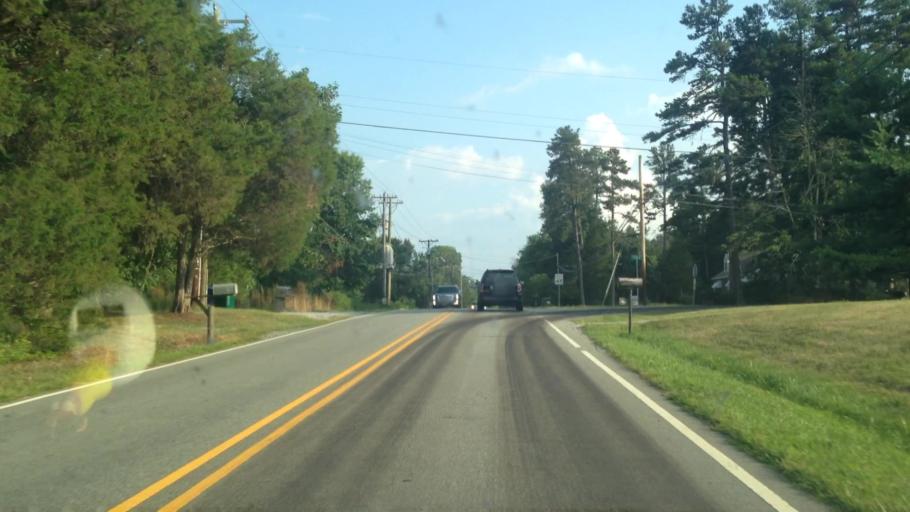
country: US
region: North Carolina
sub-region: Guilford County
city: High Point
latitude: 36.0099
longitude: -80.0606
